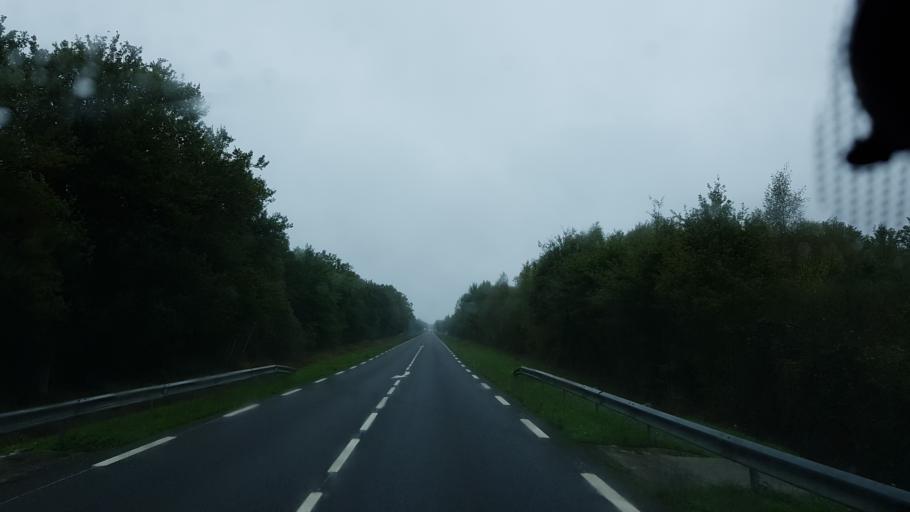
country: FR
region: Centre
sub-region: Departement du Loir-et-Cher
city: Salbris
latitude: 47.4726
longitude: 2.0407
